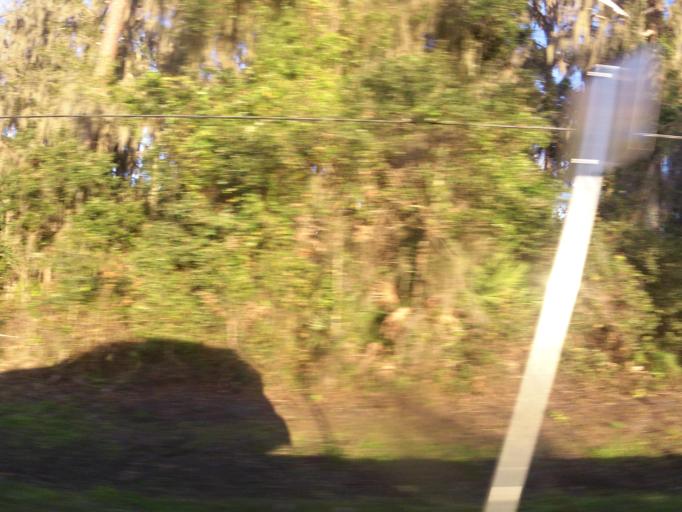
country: US
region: Florida
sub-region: Putnam County
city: East Palatka
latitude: 29.8043
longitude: -81.5503
